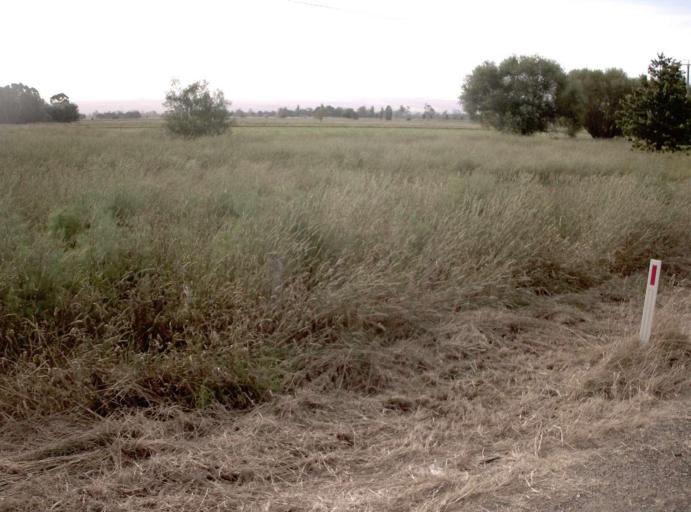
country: AU
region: Victoria
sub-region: Wellington
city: Heyfield
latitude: -38.0016
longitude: 146.7801
